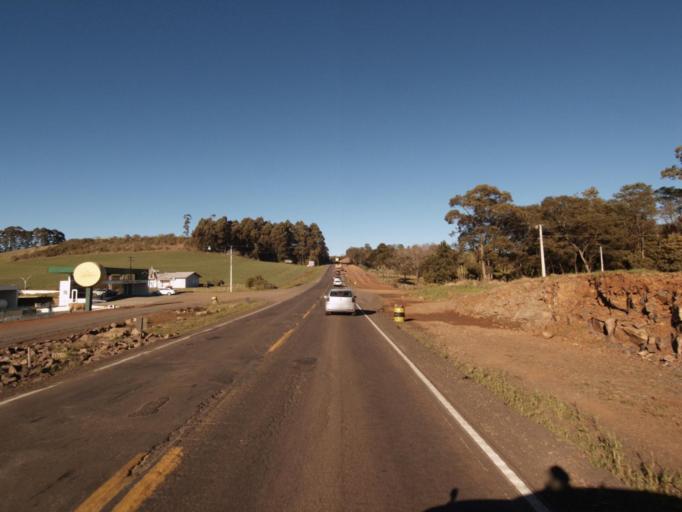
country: AR
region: Misiones
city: Bernardo de Irigoyen
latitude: -26.6290
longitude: -53.5169
